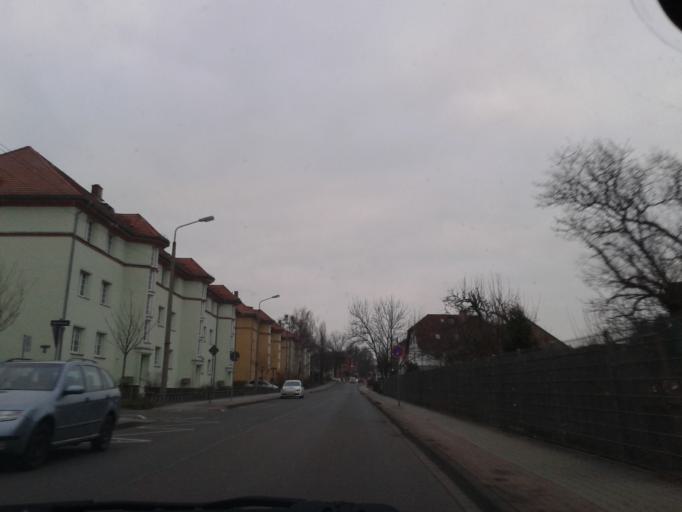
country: DE
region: Saxony
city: Dresden
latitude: 51.0113
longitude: 13.7868
